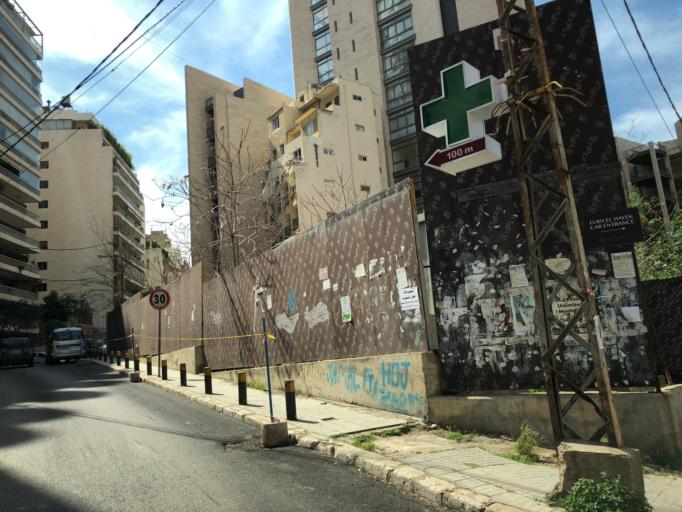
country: LB
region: Beyrouth
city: Beirut
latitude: 33.8891
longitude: 35.5169
